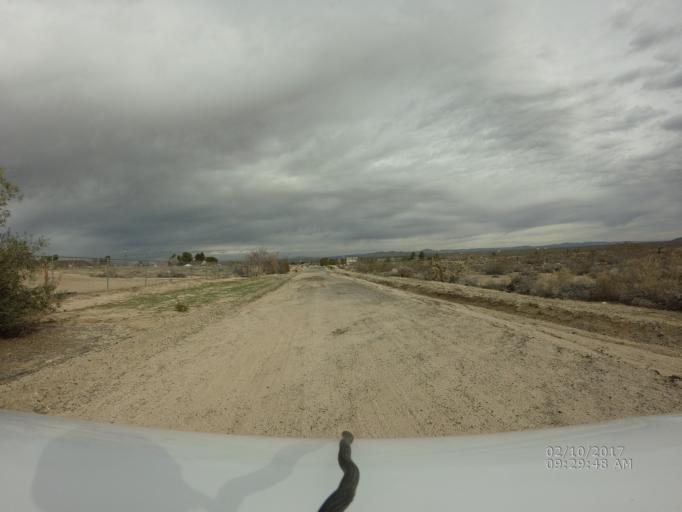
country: US
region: California
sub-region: Los Angeles County
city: Littlerock
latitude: 34.4924
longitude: -117.8900
